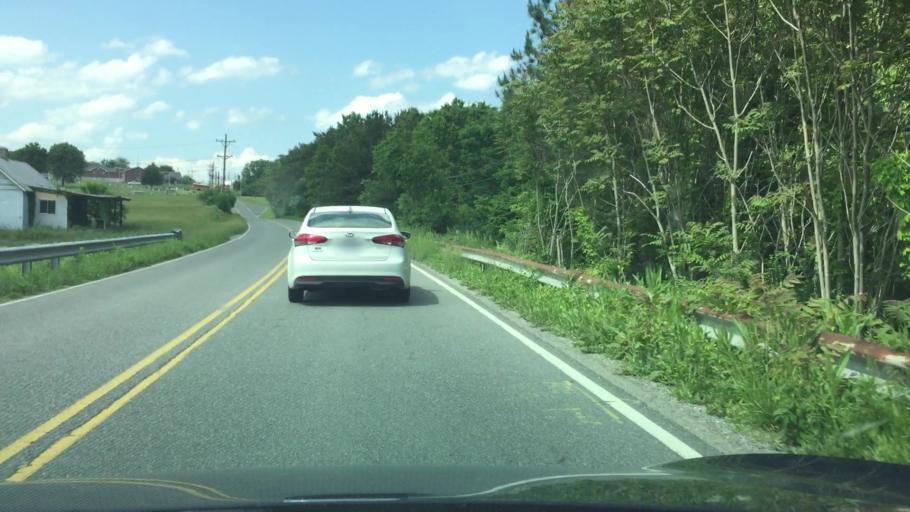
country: US
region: Virginia
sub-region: Pulaski County
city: Dublin
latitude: 37.0814
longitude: -80.6831
